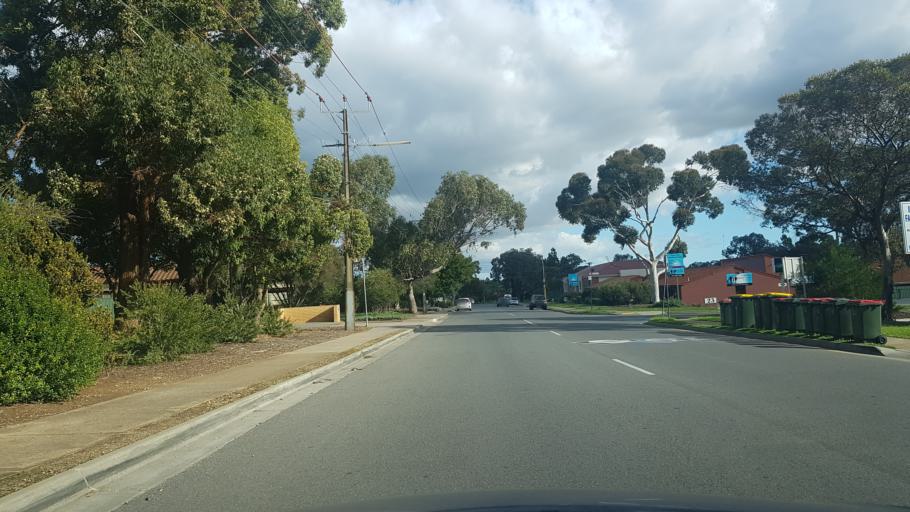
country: AU
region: South Australia
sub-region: Salisbury
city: Ingle Farm
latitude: -34.8301
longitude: 138.6509
